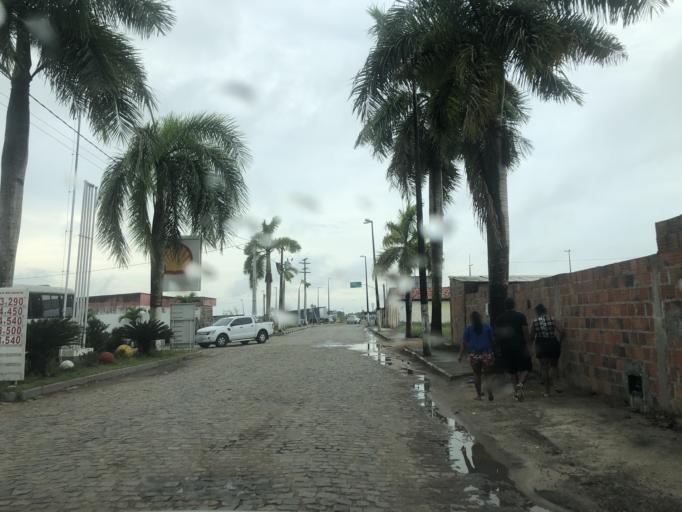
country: BR
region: Bahia
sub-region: Esplanada
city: Esplanada
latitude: -11.7956
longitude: -37.9543
